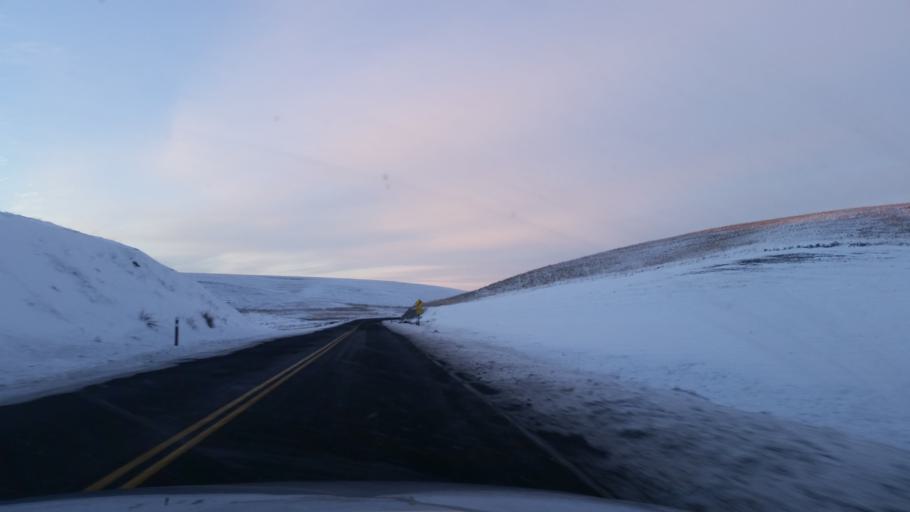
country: US
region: Washington
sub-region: Spokane County
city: Cheney
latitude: 47.1975
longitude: -117.8799
